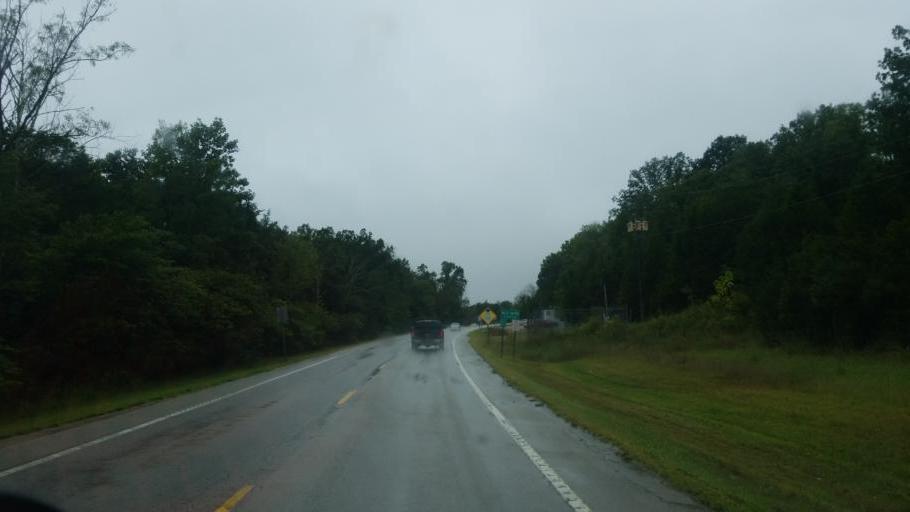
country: US
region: Ohio
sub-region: Adams County
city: West Union
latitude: 38.7952
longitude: -83.5193
